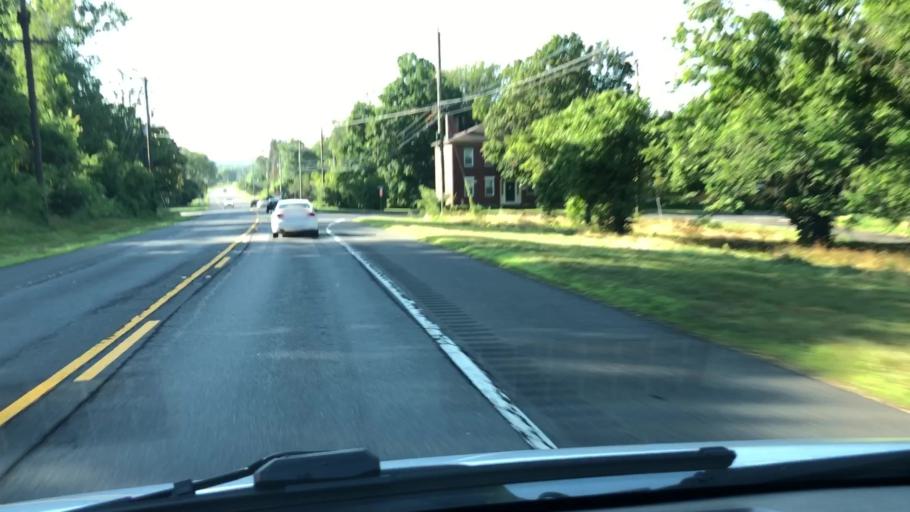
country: US
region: Massachusetts
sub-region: Hampshire County
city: North Amherst
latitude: 42.4327
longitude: -72.5452
